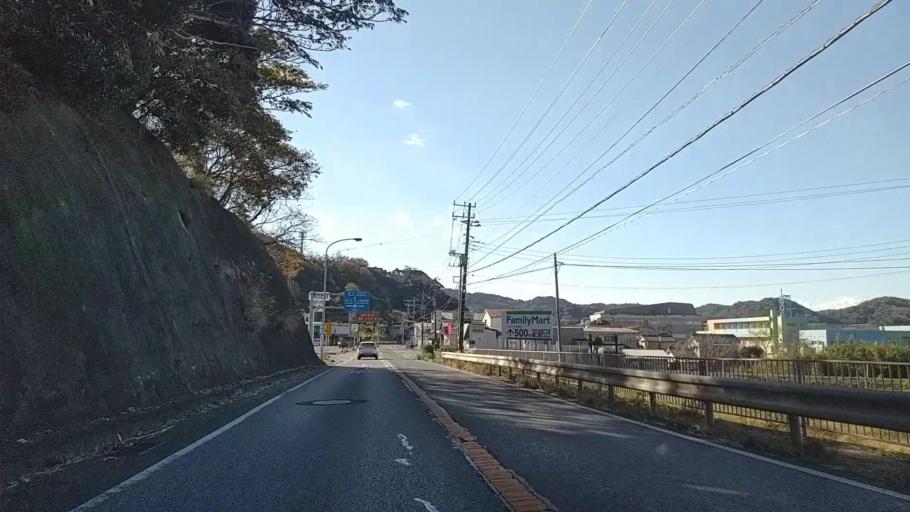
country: JP
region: Chiba
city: Futtsu
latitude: 35.2250
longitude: 139.8738
